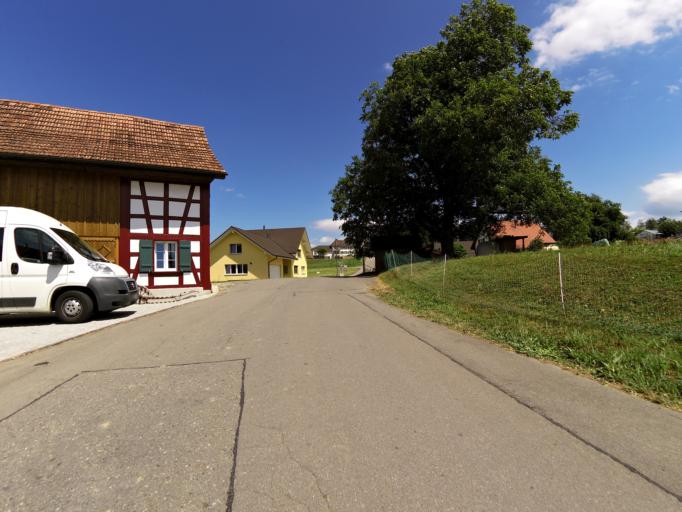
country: CH
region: Thurgau
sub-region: Weinfelden District
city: Maerstetten-Dorf
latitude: 47.6002
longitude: 9.0544
